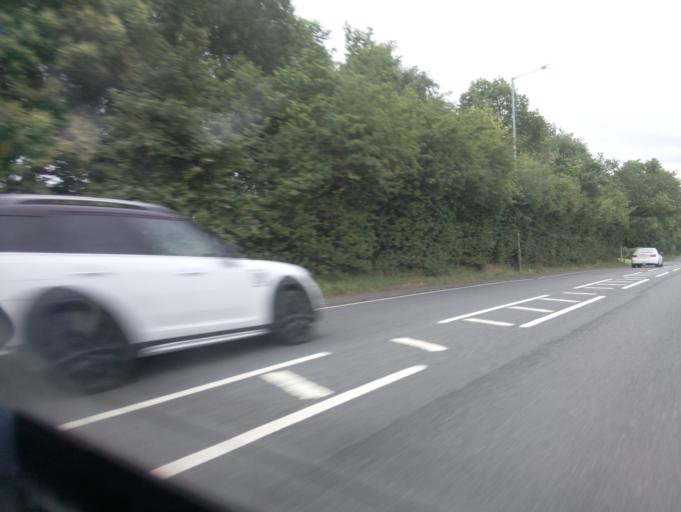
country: GB
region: England
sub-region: Worcestershire
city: Droitwich
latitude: 52.2963
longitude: -2.1100
